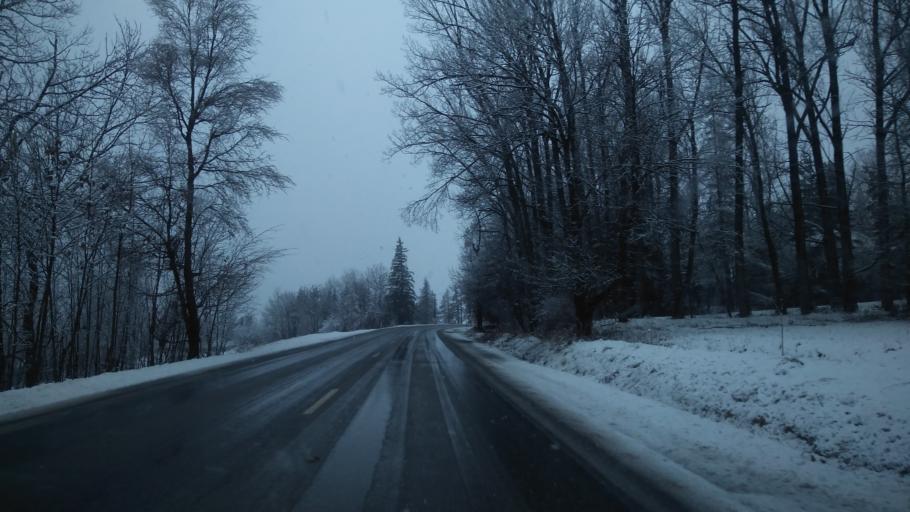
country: FR
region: Provence-Alpes-Cote d'Azur
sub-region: Departement des Hautes-Alpes
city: Le Monetier-les-Bains
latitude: 44.9784
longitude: 6.5022
